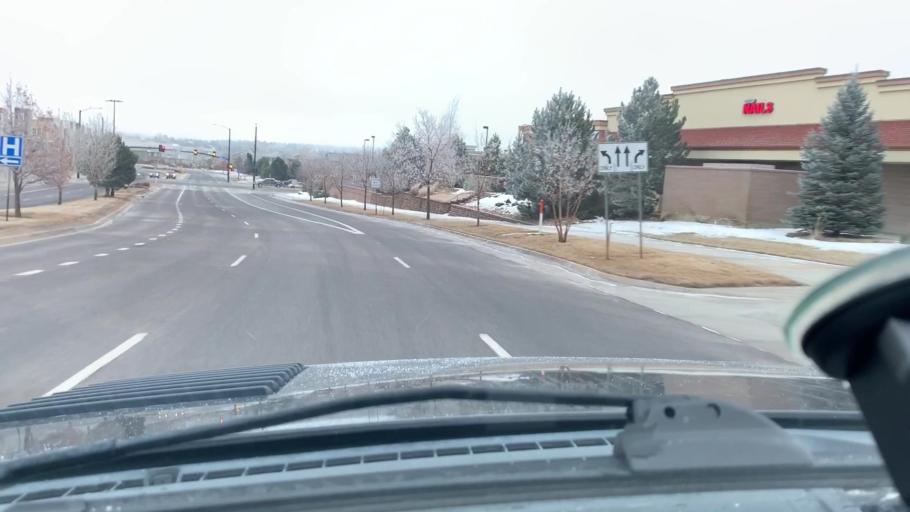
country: US
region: Colorado
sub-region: Arapahoe County
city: Dove Valley
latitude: 39.5756
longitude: -104.8088
